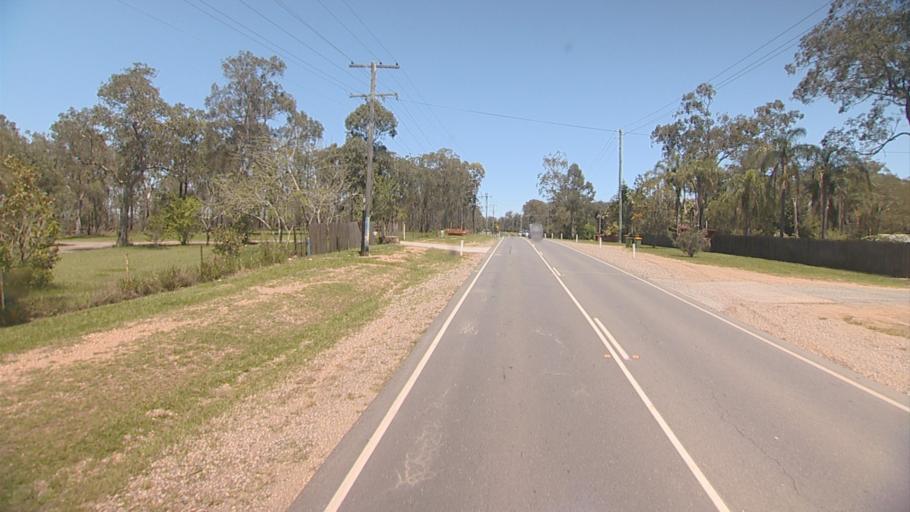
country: AU
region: Queensland
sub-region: Logan
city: Park Ridge South
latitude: -27.7056
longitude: 153.0051
